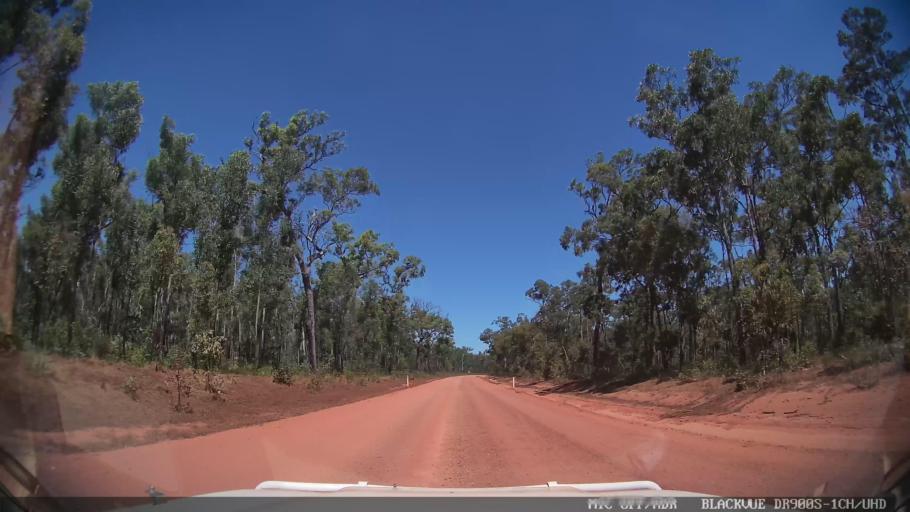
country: AU
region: Queensland
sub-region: Torres
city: Thursday Island
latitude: -11.1827
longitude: 142.2542
